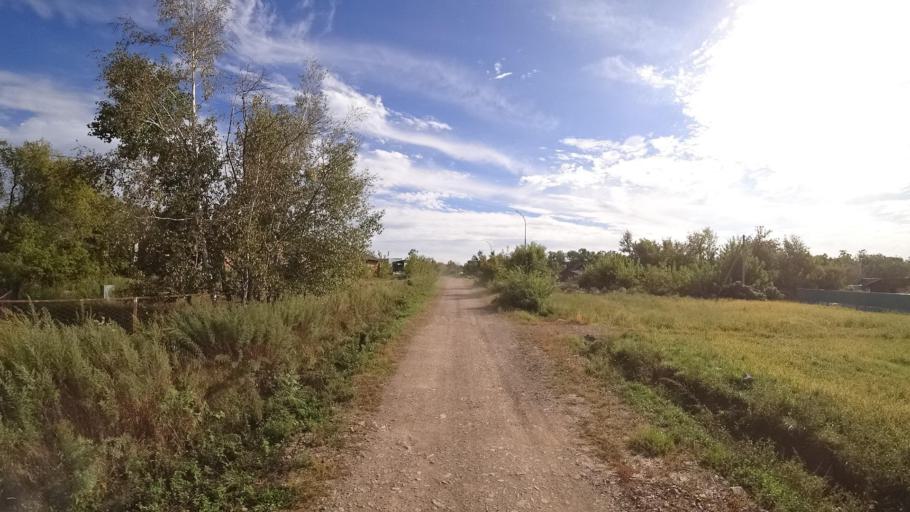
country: RU
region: Primorskiy
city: Dostoyevka
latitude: 44.3035
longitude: 133.4554
